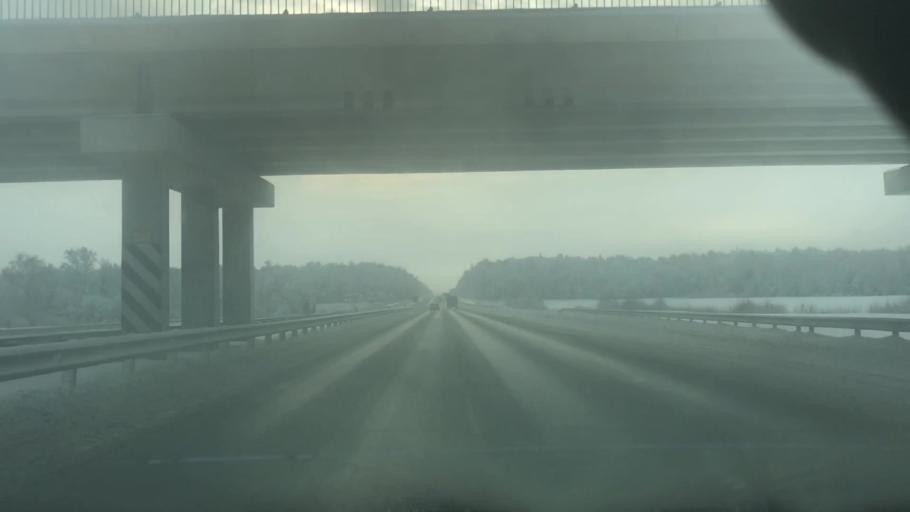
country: RU
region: Tula
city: Venev
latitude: 54.3752
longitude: 38.1549
